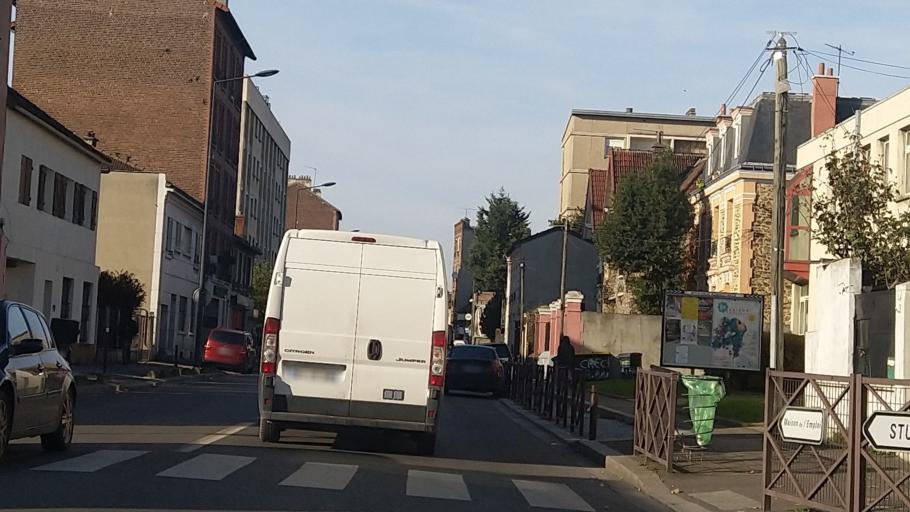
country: FR
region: Ile-de-France
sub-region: Departement de Seine-Saint-Denis
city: Stains
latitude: 48.9610
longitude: 2.3814
